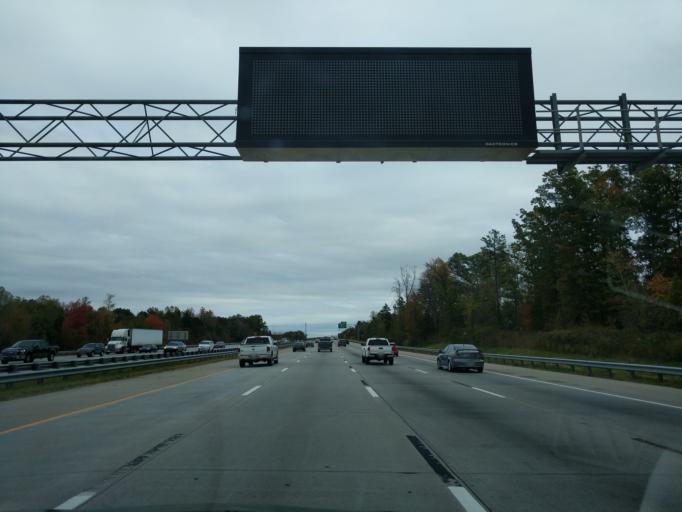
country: US
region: North Carolina
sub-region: Rowan County
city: East Spencer
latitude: 35.6677
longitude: -80.4385
